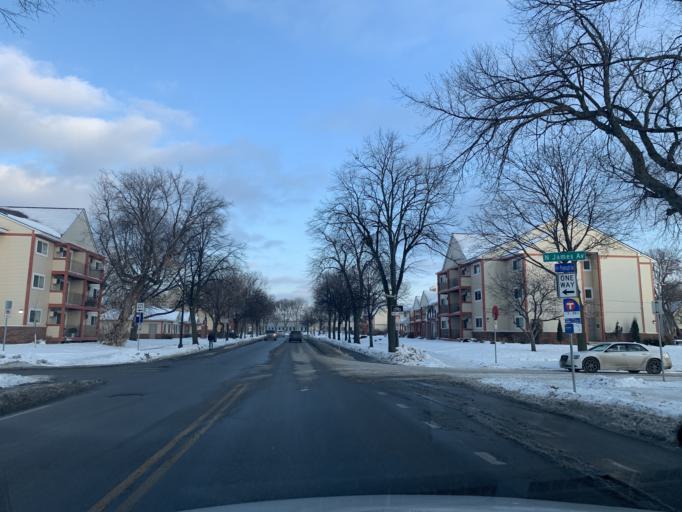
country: US
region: Minnesota
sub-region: Hennepin County
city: Minneapolis
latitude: 44.9915
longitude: -93.3011
